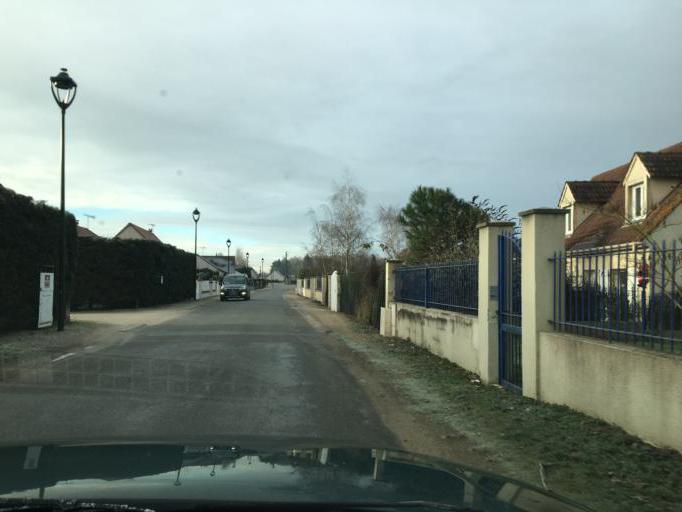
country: FR
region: Centre
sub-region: Departement du Loiret
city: Dry
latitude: 47.8014
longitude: 1.7207
